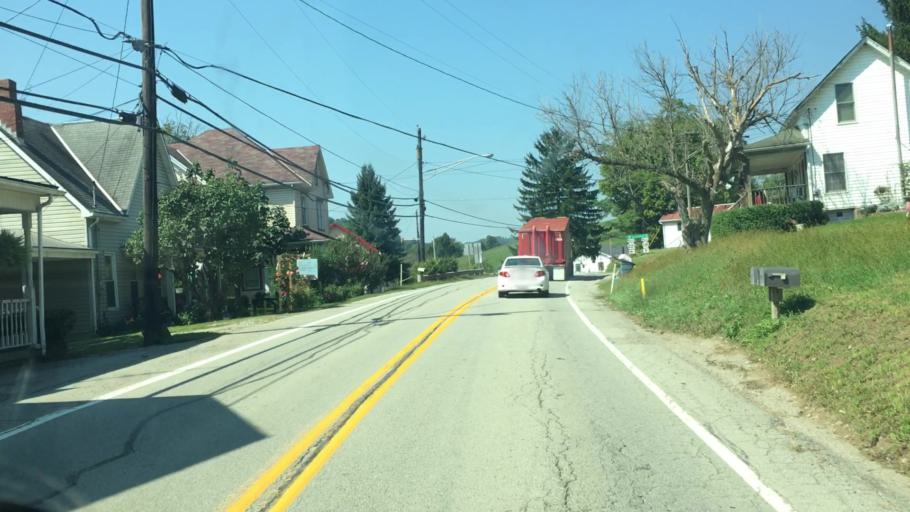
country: US
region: Pennsylvania
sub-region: Washington County
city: Washington
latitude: 40.0469
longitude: -80.2940
